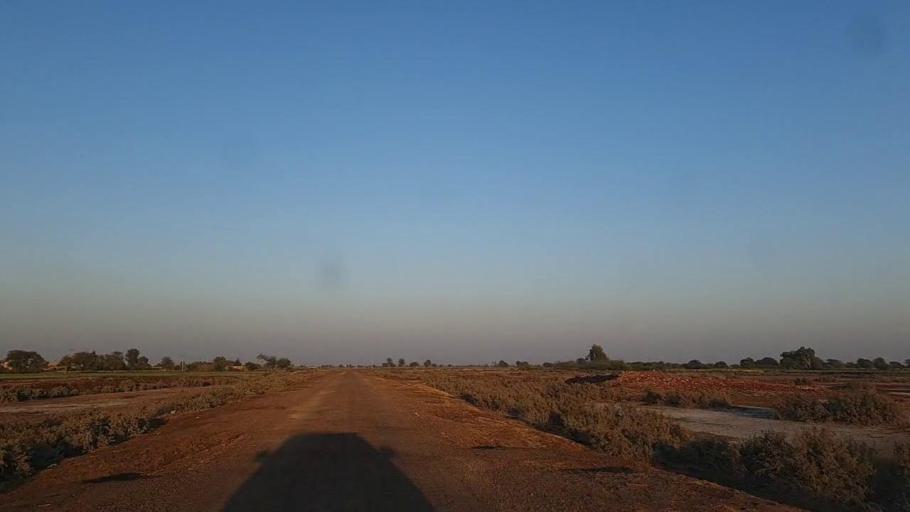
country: PK
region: Sindh
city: Samaro
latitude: 25.3000
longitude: 69.3927
